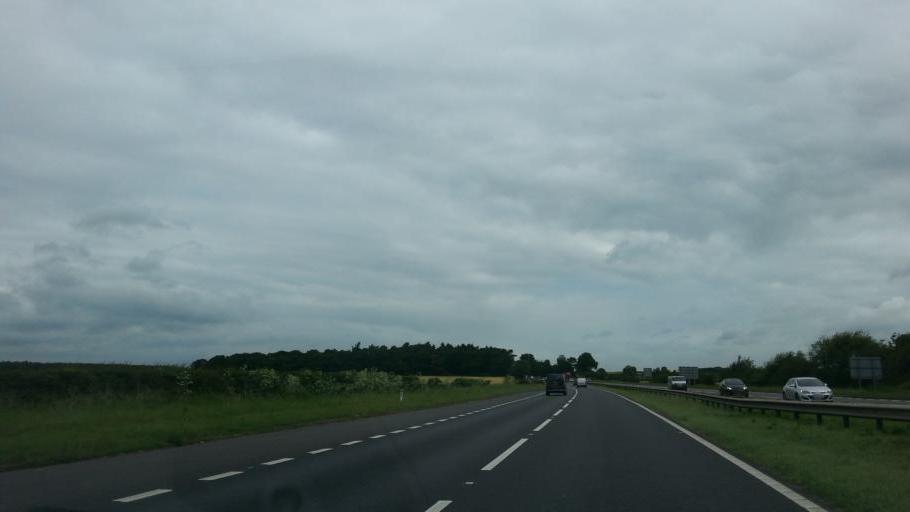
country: GB
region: England
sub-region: Nottinghamshire
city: Babworth
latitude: 53.3450
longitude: -1.0310
